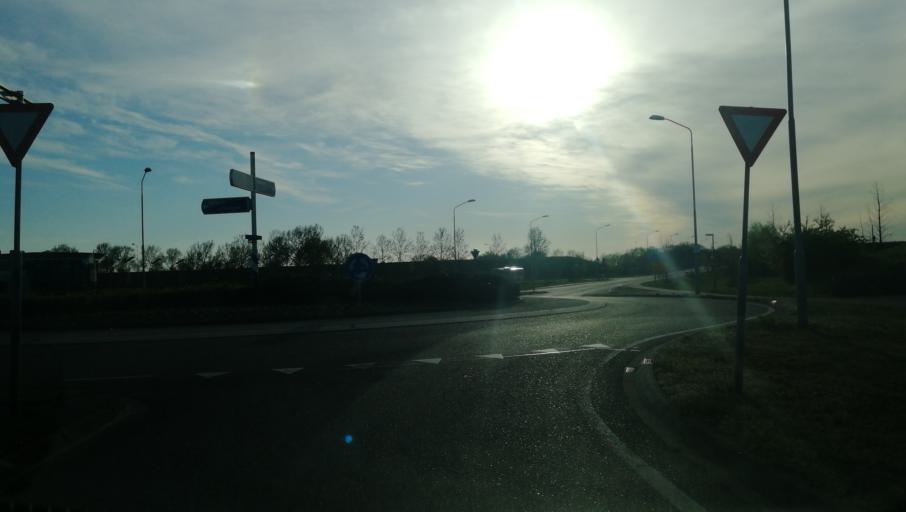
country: NL
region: Limburg
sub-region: Gemeente Venlo
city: Tegelen
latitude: 51.3711
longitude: 6.1266
